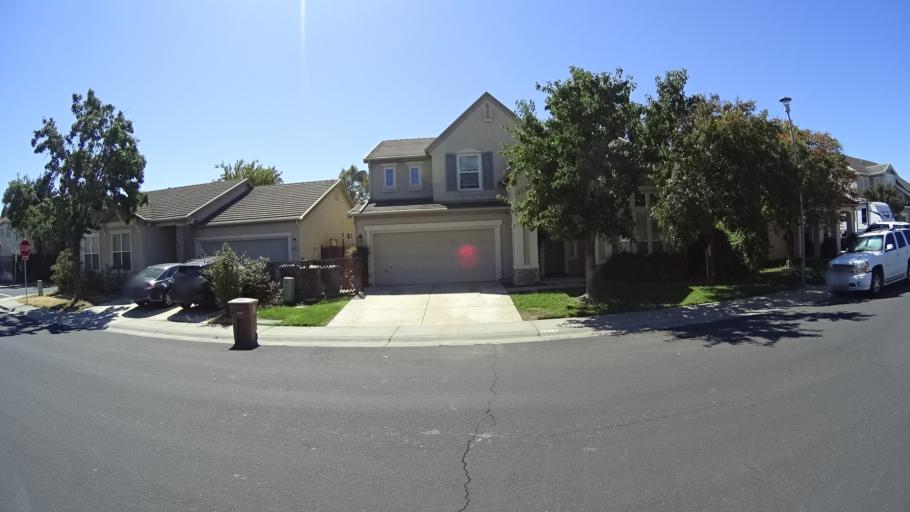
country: US
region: California
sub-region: Sacramento County
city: Elk Grove
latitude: 38.4120
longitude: -121.3471
